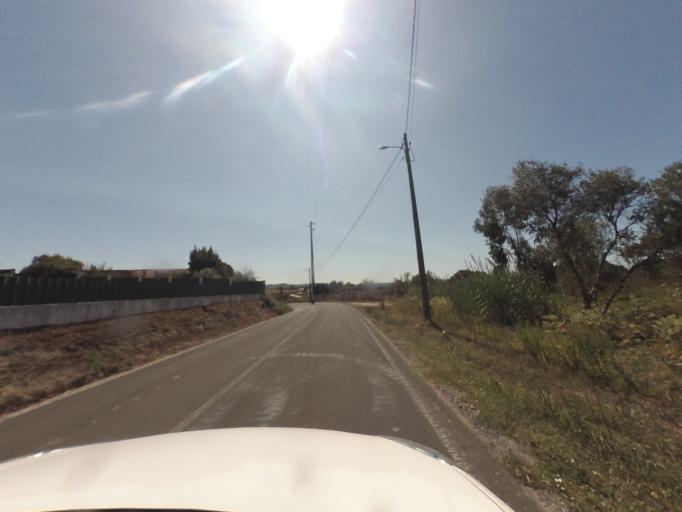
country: PT
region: Leiria
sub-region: Alcobaca
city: Alcobaca
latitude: 39.5084
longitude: -8.9737
